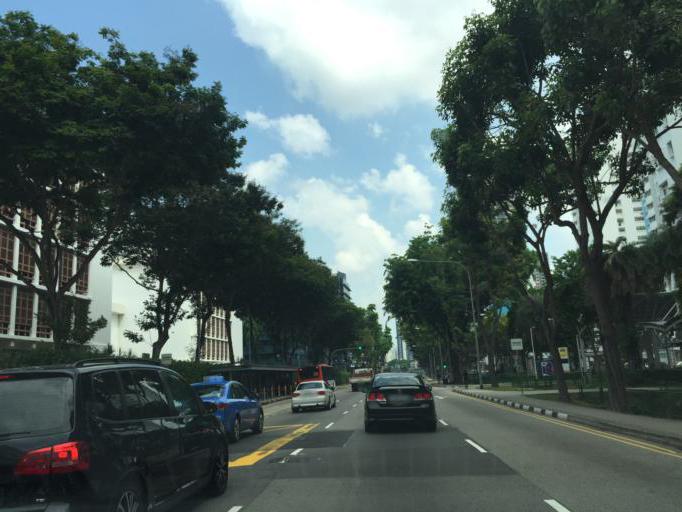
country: SG
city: Singapore
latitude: 1.3190
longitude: 103.8641
